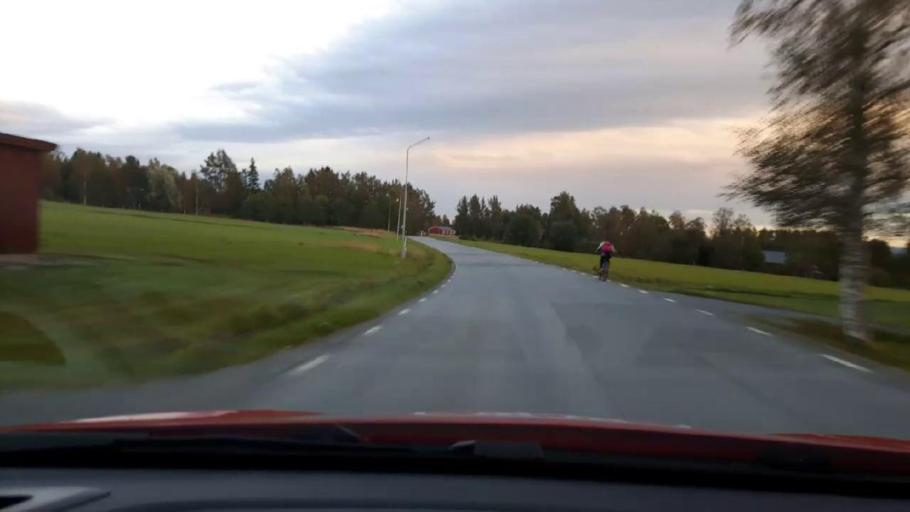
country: SE
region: Jaemtland
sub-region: OEstersunds Kommun
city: Ostersund
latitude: 63.0467
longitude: 14.4534
